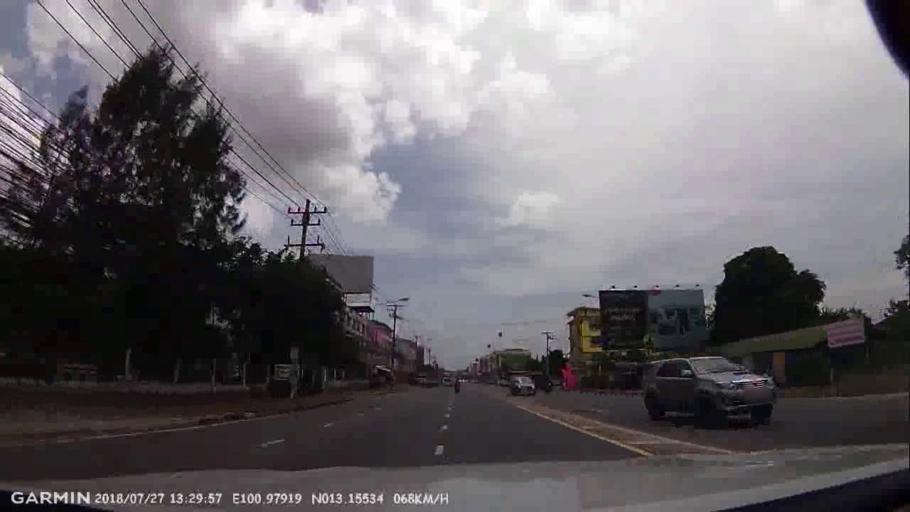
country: TH
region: Chon Buri
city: Si Racha
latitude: 13.1554
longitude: 100.9791
